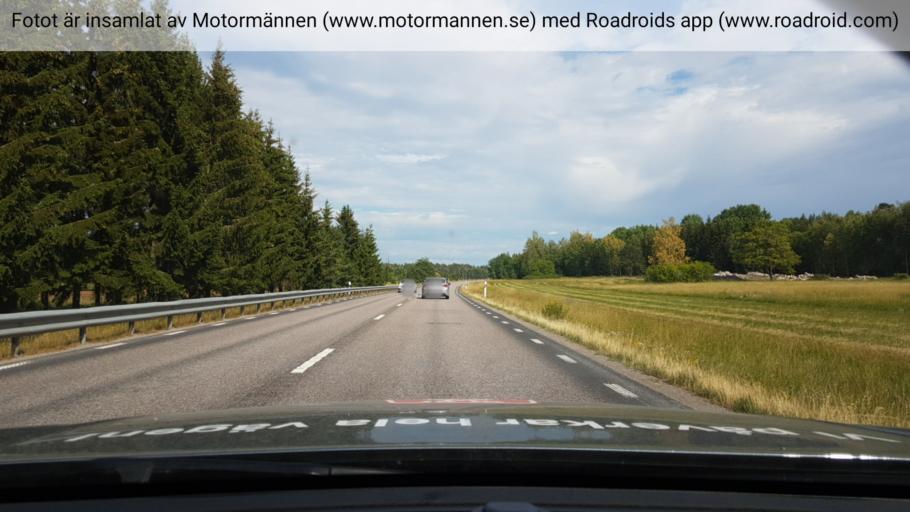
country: SE
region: Uppsala
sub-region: Enkopings Kommun
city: Orsundsbro
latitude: 59.8593
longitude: 17.3909
